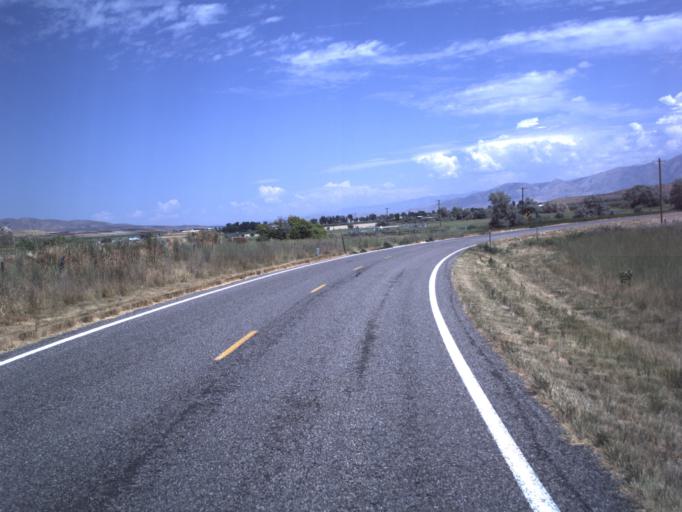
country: US
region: Utah
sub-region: Box Elder County
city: Tremonton
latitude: 41.6363
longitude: -112.3295
